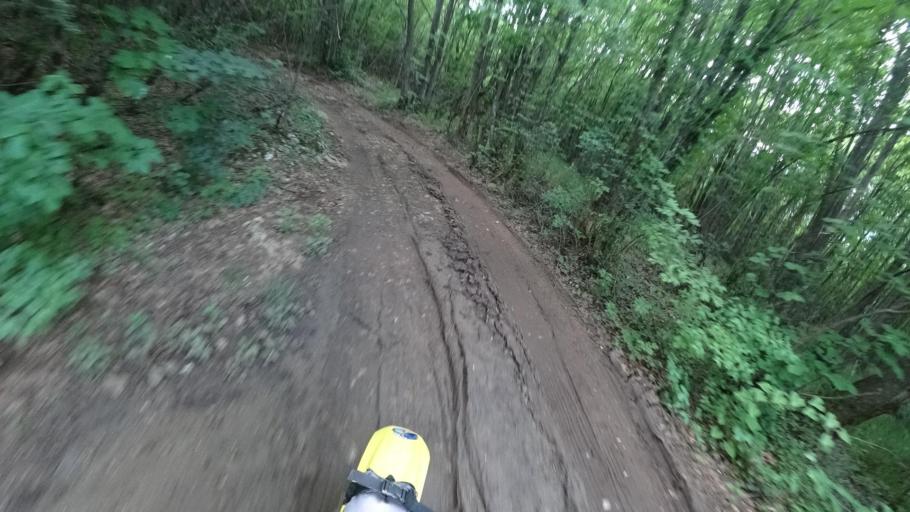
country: BA
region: Federation of Bosnia and Herzegovina
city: Bihac
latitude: 44.8124
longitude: 15.9239
